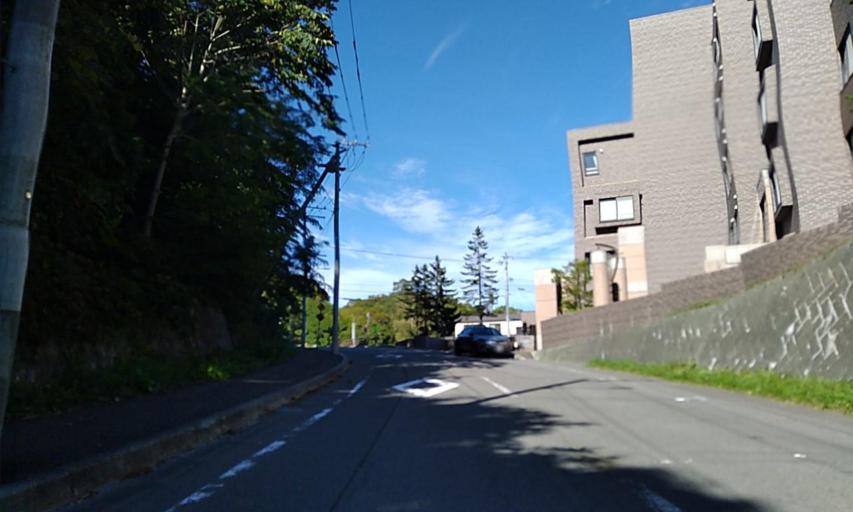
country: JP
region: Hokkaido
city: Sapporo
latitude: 43.0476
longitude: 141.2917
